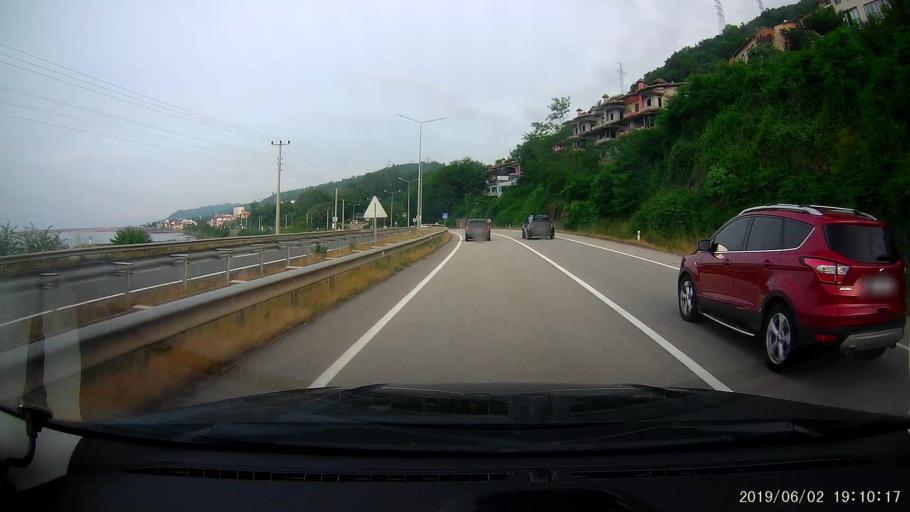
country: TR
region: Ordu
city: Gulyali
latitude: 40.9702
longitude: 38.0421
